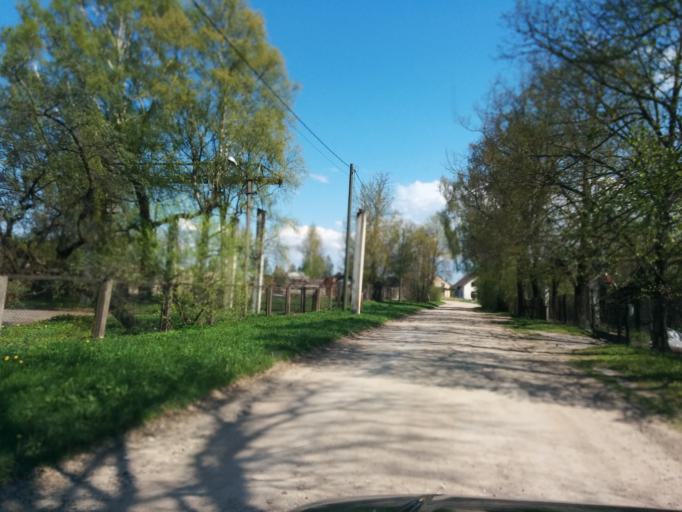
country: LV
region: Jelgava
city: Jelgava
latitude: 56.6305
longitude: 23.7066
